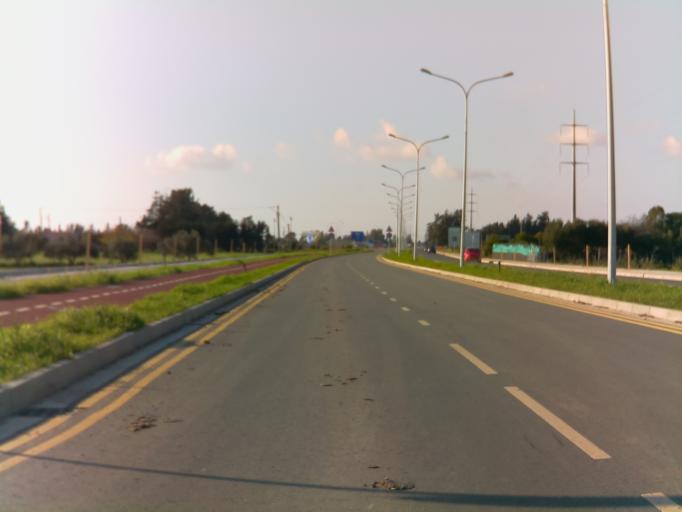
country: CY
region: Pafos
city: Paphos
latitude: 34.7379
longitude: 32.4553
